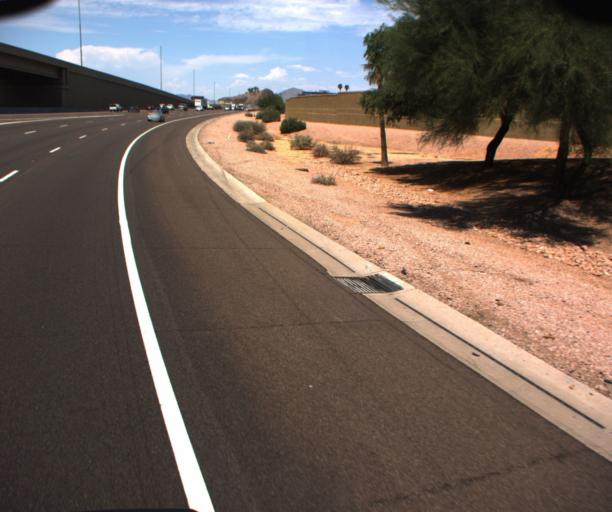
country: US
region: Arizona
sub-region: Maricopa County
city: Guadalupe
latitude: 33.3900
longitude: -111.9672
